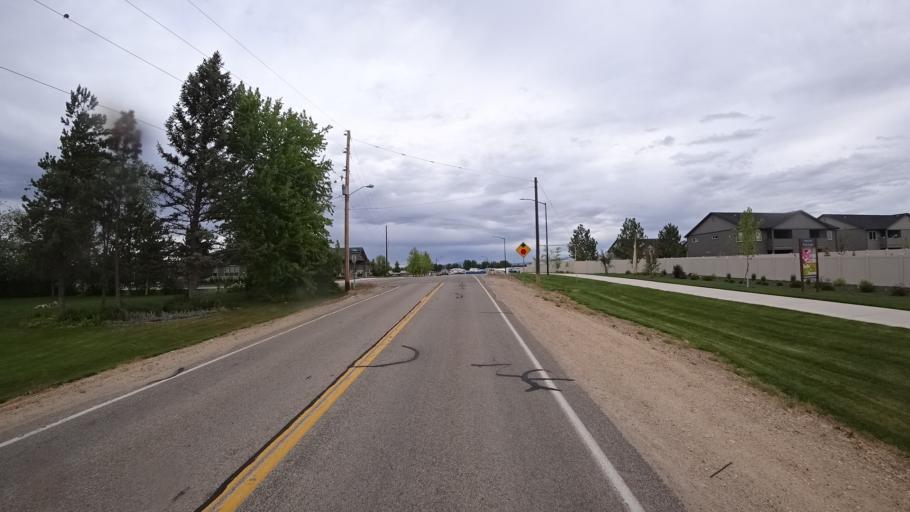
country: US
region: Idaho
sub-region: Ada County
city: Meridian
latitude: 43.5880
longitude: -116.4137
